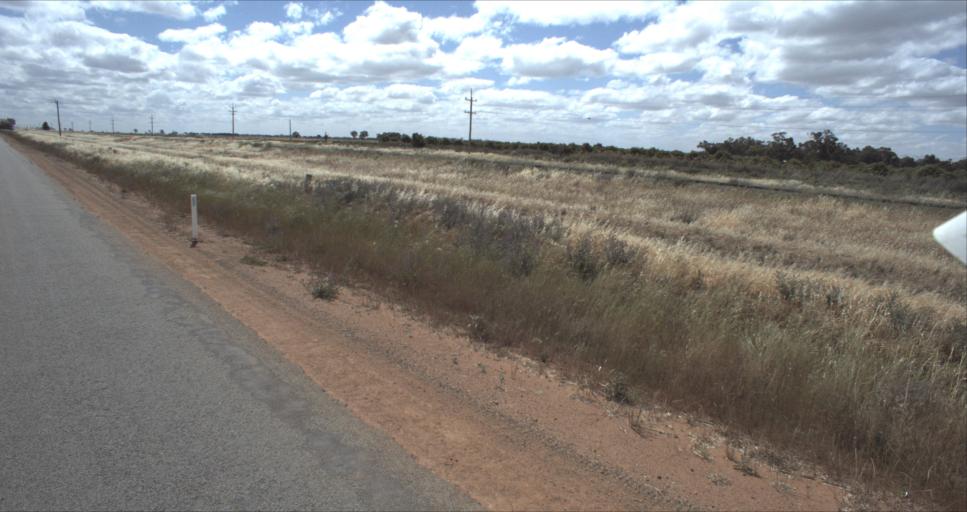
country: AU
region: New South Wales
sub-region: Leeton
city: Leeton
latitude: -34.5891
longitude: 146.3658
